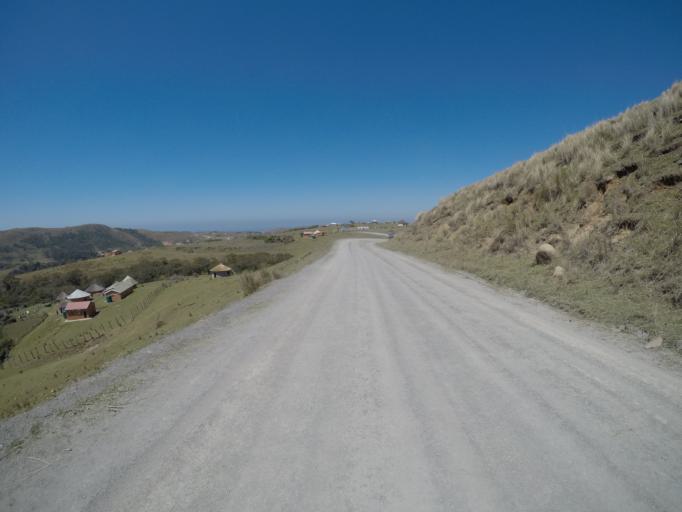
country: ZA
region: Eastern Cape
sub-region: OR Tambo District Municipality
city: Libode
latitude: -32.0142
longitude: 29.0770
